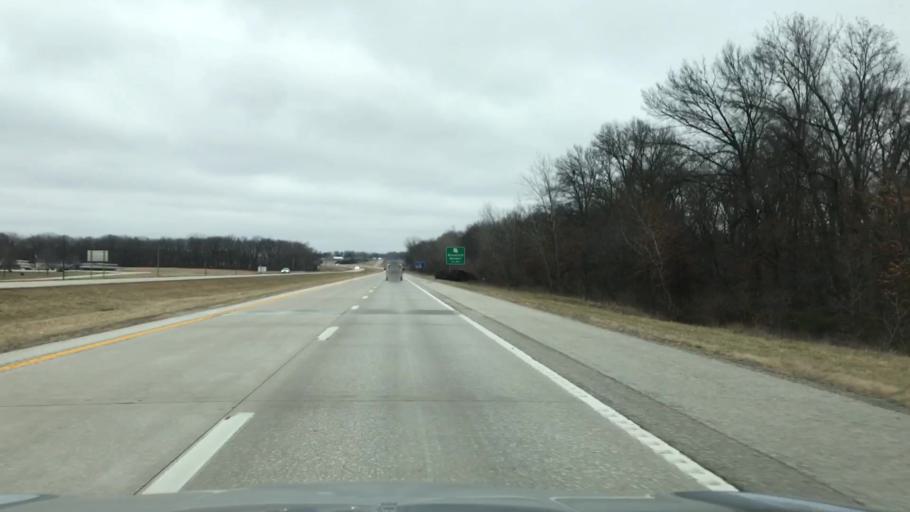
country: US
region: Missouri
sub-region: Linn County
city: Brookfield
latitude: 39.7757
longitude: -93.0900
